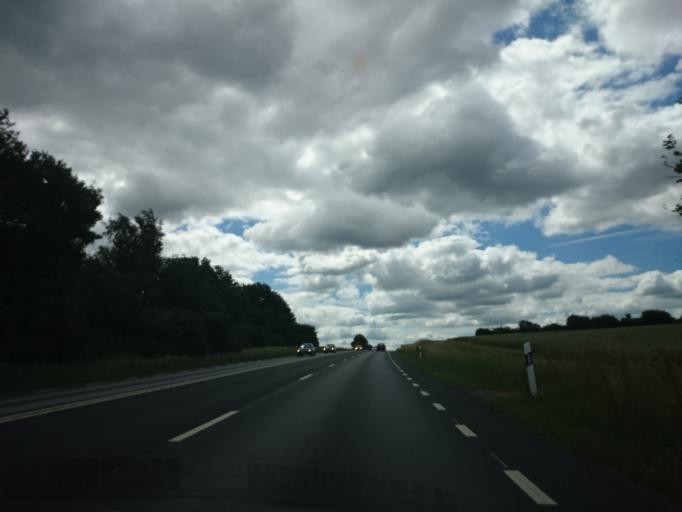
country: SE
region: Skane
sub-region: Kristianstads Kommun
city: Degeberga
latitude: 55.7956
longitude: 14.1468
